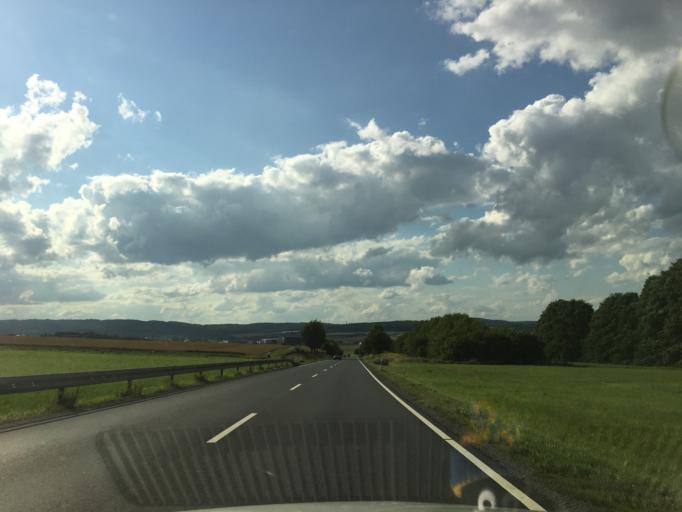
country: DE
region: Hesse
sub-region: Regierungsbezirk Darmstadt
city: Wehrheim
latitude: 50.3010
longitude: 8.5325
